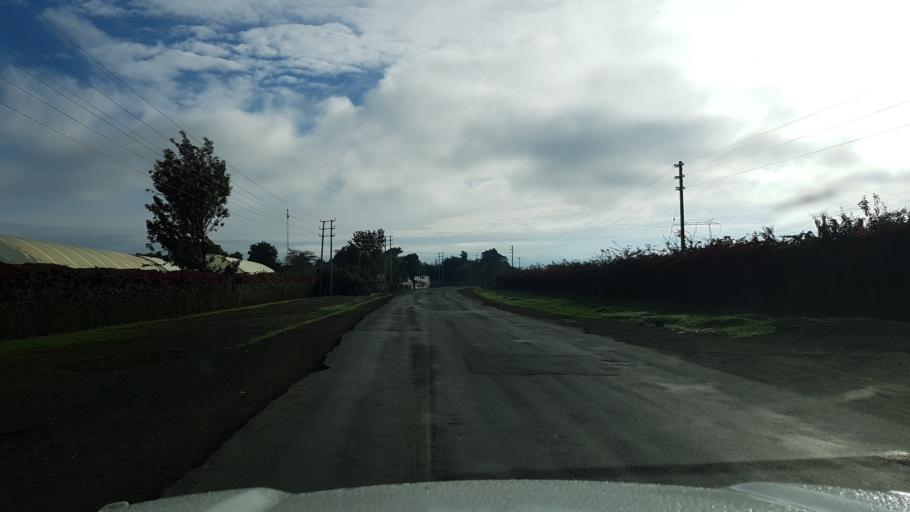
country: KE
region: Nakuru
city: Naivasha
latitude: -0.8283
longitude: 36.3734
